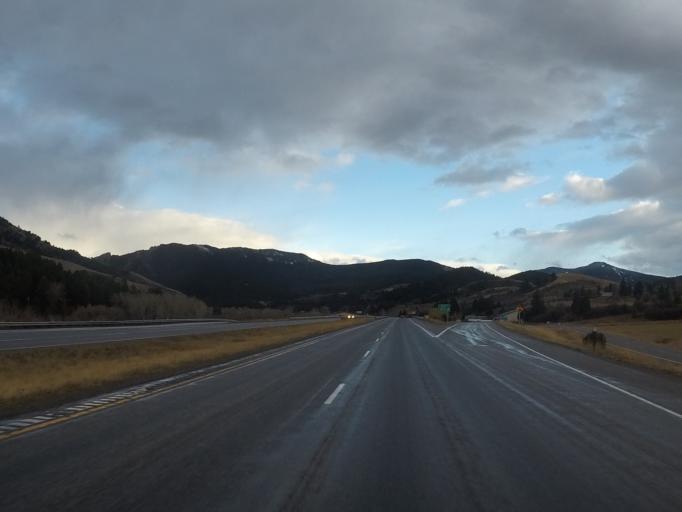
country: US
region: Montana
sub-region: Gallatin County
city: Bozeman
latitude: 45.6559
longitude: -110.9471
